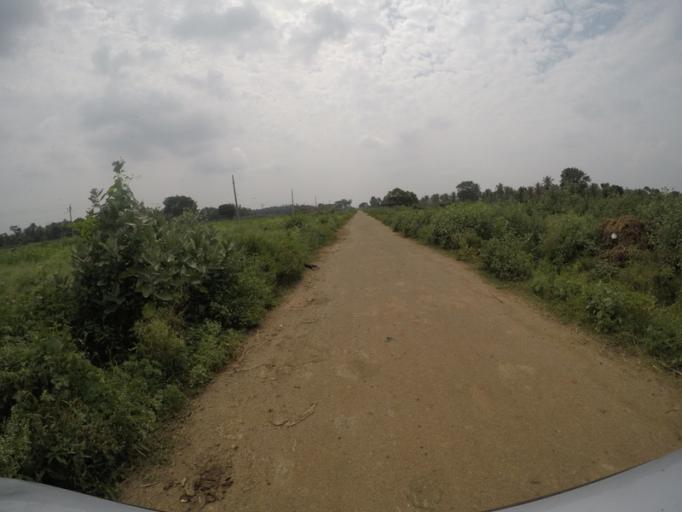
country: IN
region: Karnataka
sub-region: Mandya
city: Malavalli
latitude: 12.4137
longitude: 77.2166
